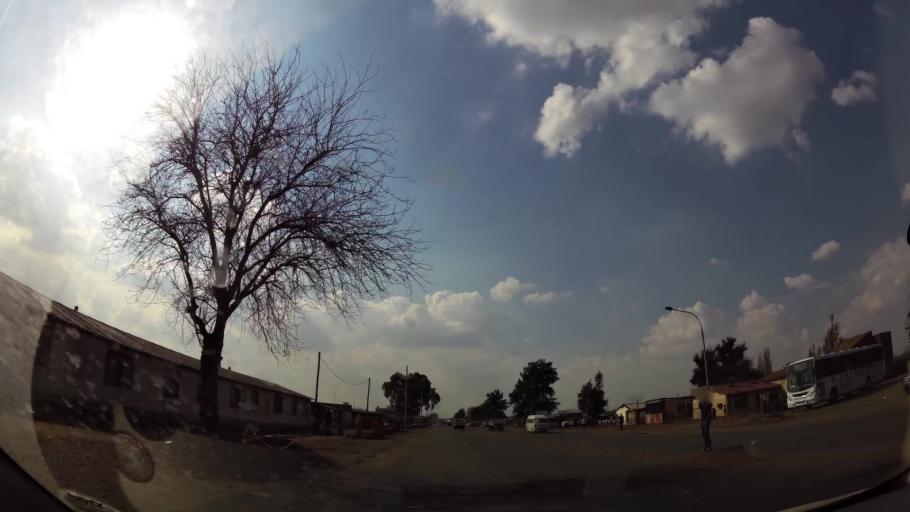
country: ZA
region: Gauteng
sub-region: Ekurhuleni Metropolitan Municipality
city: Germiston
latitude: -26.3370
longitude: 28.1408
